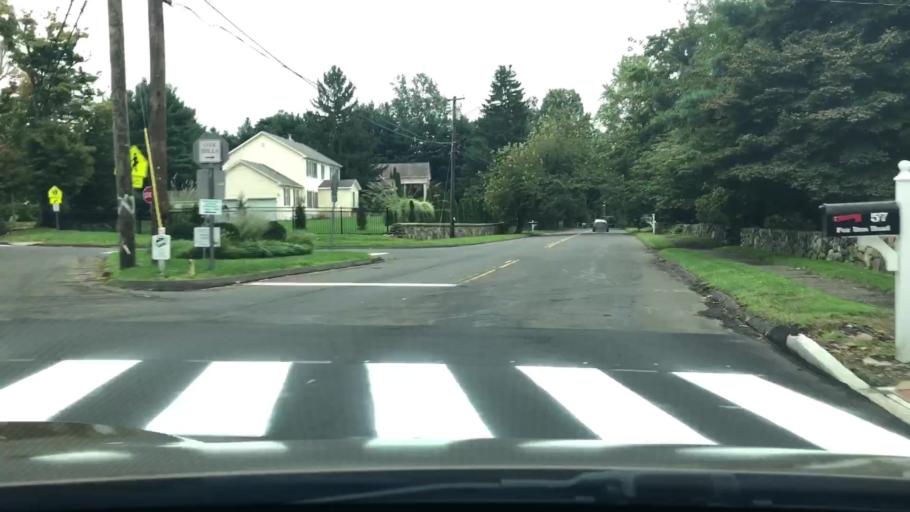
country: US
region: Connecticut
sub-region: Fairfield County
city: Norwalk
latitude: 41.1265
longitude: -73.4525
